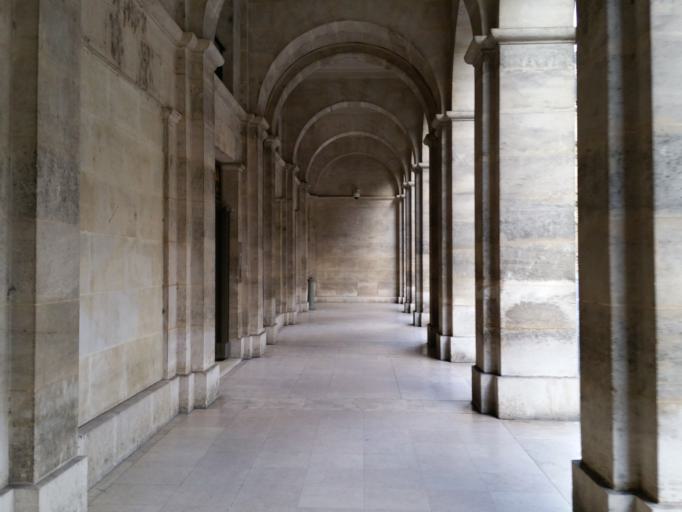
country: FR
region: Ile-de-France
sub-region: Paris
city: Paris
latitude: 48.8493
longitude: 2.3366
